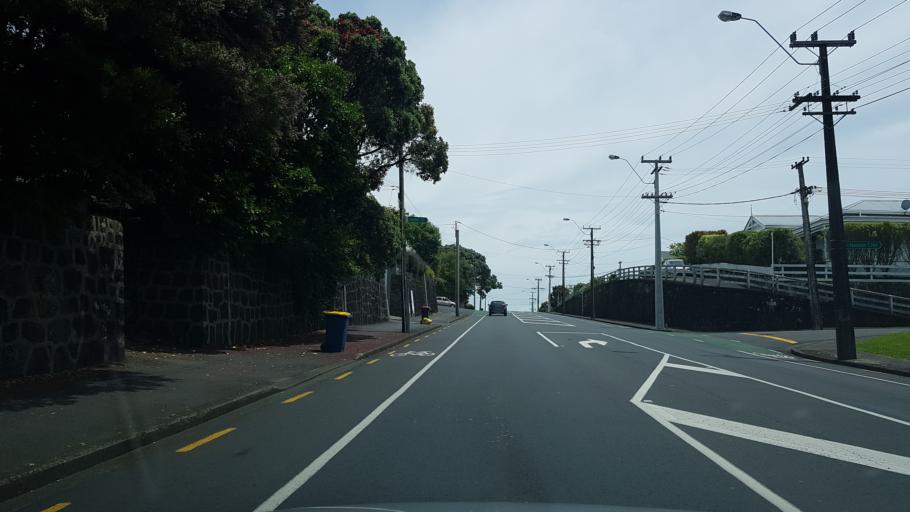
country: NZ
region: Auckland
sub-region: Auckland
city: North Shore
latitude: -36.8156
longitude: 174.7935
